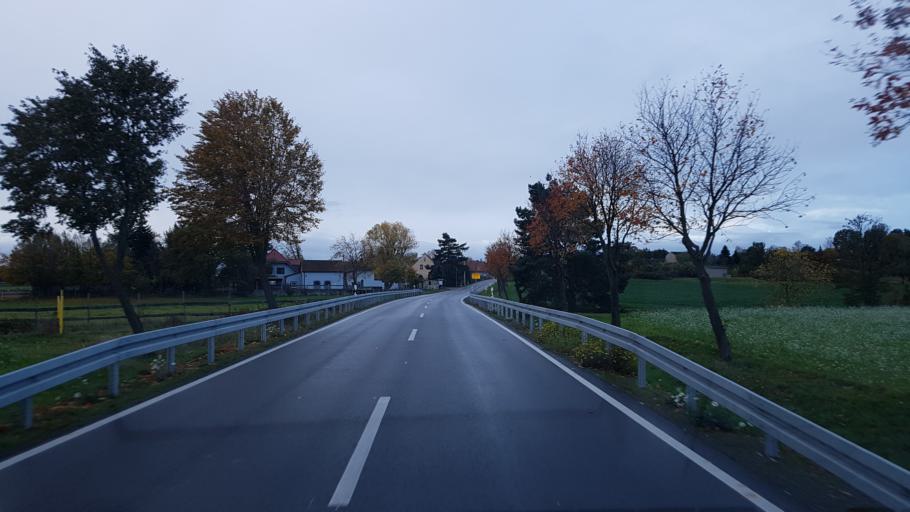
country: DE
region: Saxony
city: Belgern
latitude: 51.4546
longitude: 13.1156
